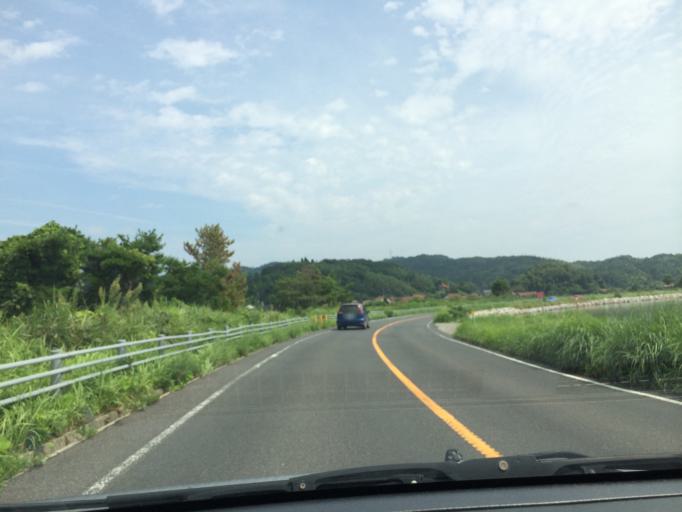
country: JP
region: Shimane
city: Sakaiminato
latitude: 35.5370
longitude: 133.1563
